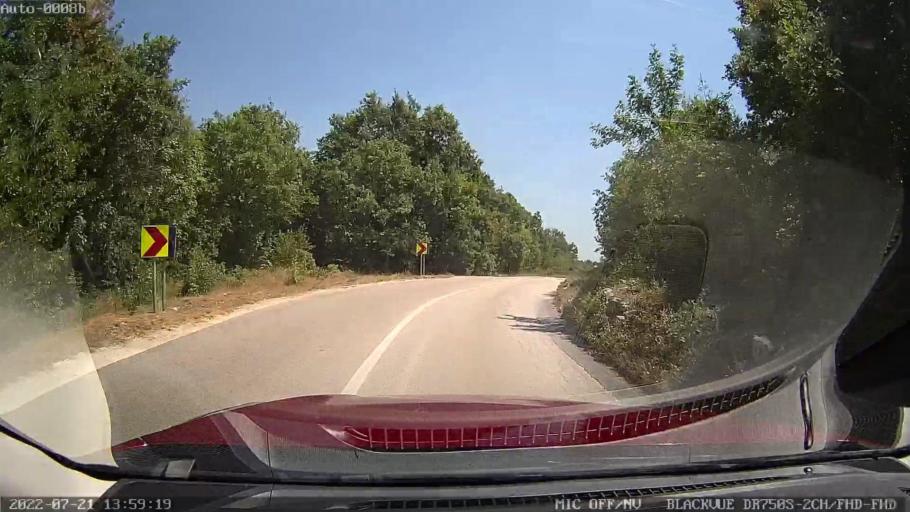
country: HR
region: Istarska
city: Vodnjan
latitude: 45.1053
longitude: 13.8613
